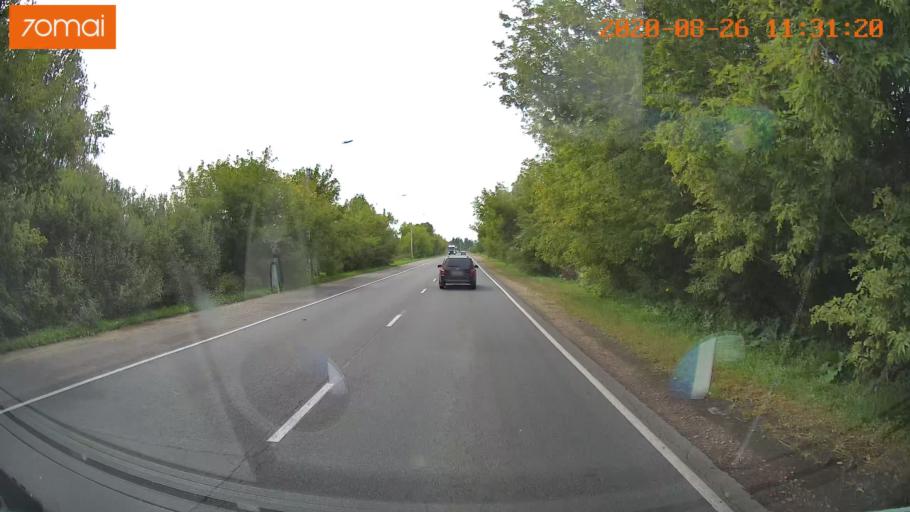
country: RU
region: Rjazan
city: Shilovo
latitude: 54.3072
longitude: 40.8746
